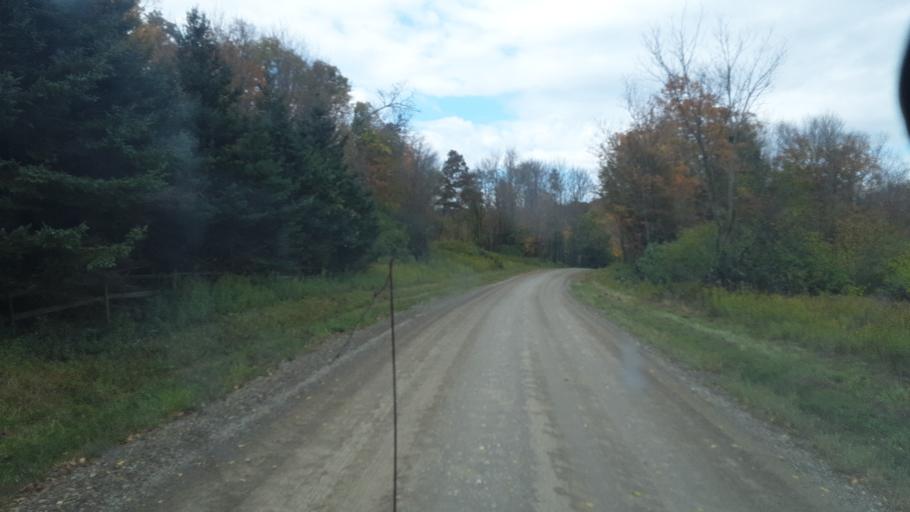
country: US
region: New York
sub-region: Allegany County
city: Alfred
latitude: 42.3783
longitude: -77.8525
